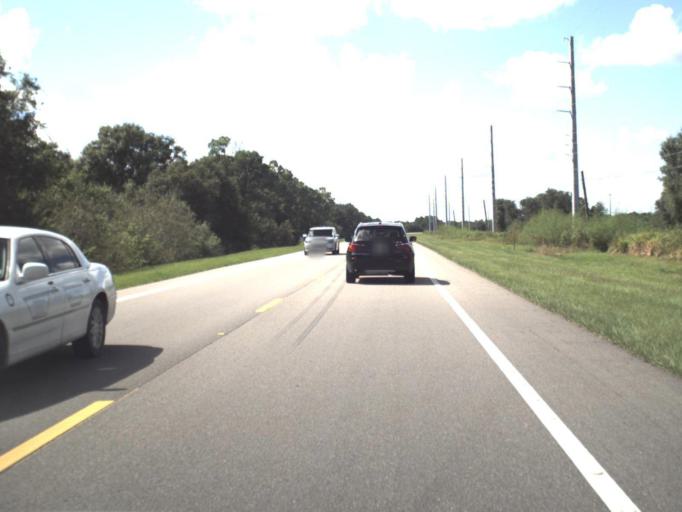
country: US
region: Florida
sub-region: Sarasota County
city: The Meadows
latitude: 27.4171
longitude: -82.3572
